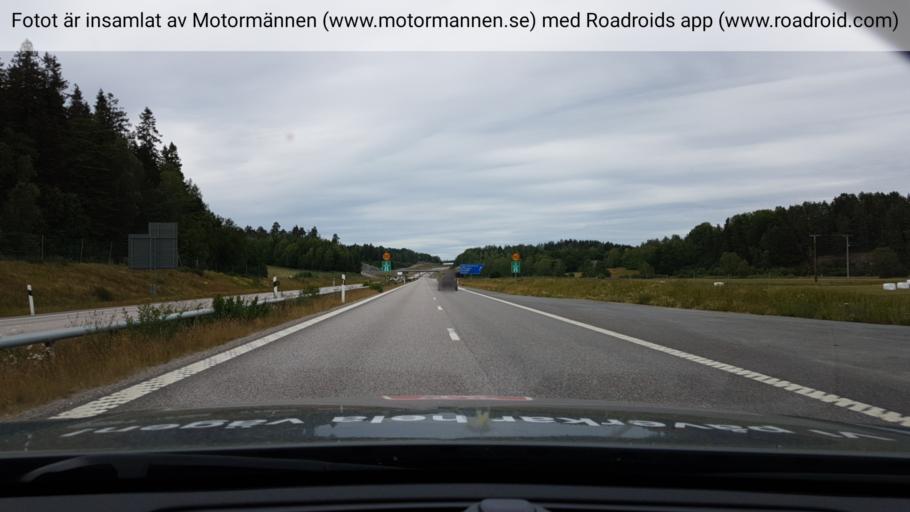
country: SE
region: Stockholm
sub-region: Nynashamns Kommun
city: Osmo
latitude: 58.9700
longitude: 17.9090
